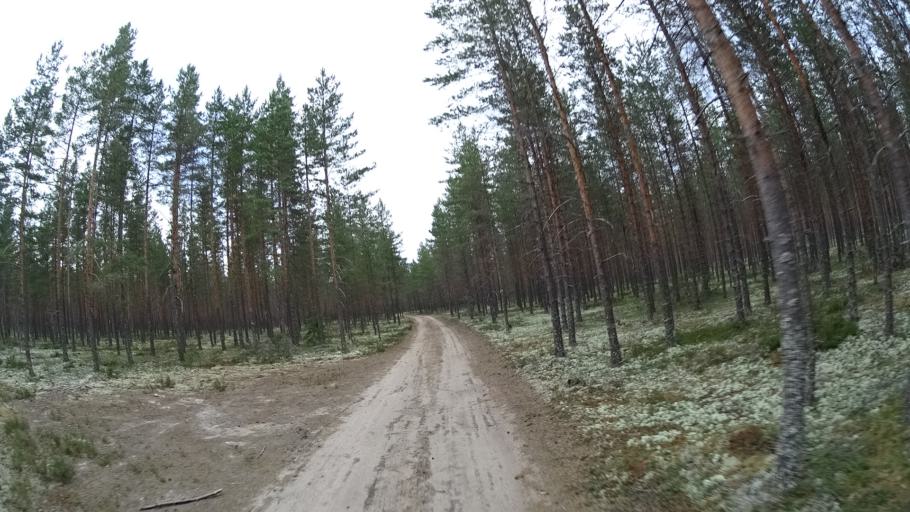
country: FI
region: Satakunta
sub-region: Pohjois-Satakunta
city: Jaemijaervi
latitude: 61.7658
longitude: 22.7871
